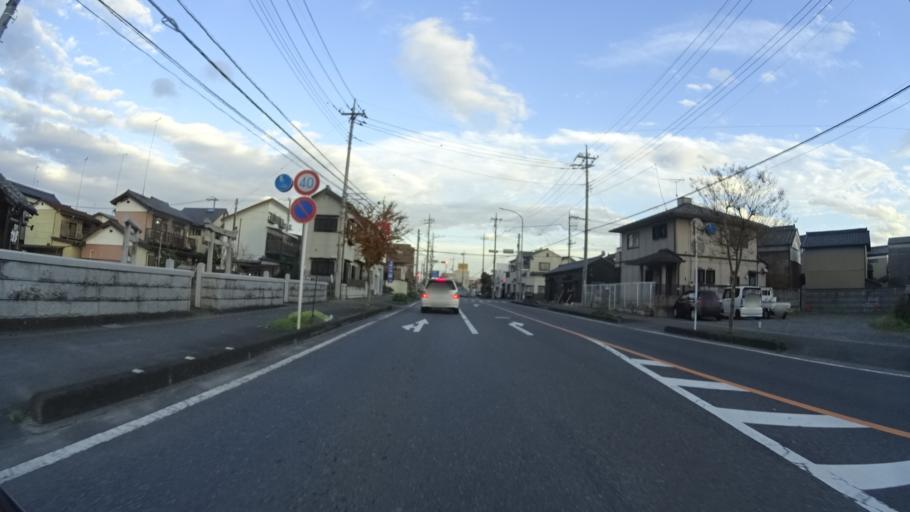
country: JP
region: Tochigi
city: Tochigi
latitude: 36.3906
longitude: 139.7337
